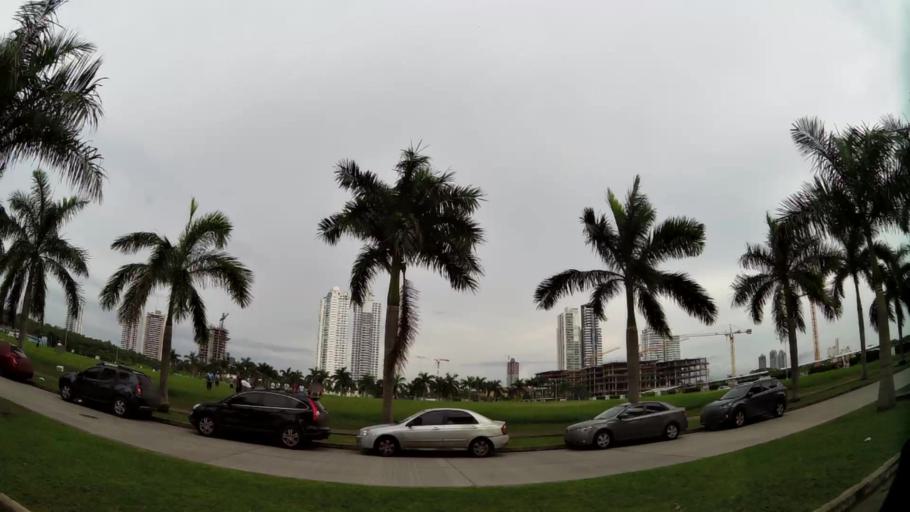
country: PA
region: Panama
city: San Miguelito
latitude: 9.0115
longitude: -79.4660
